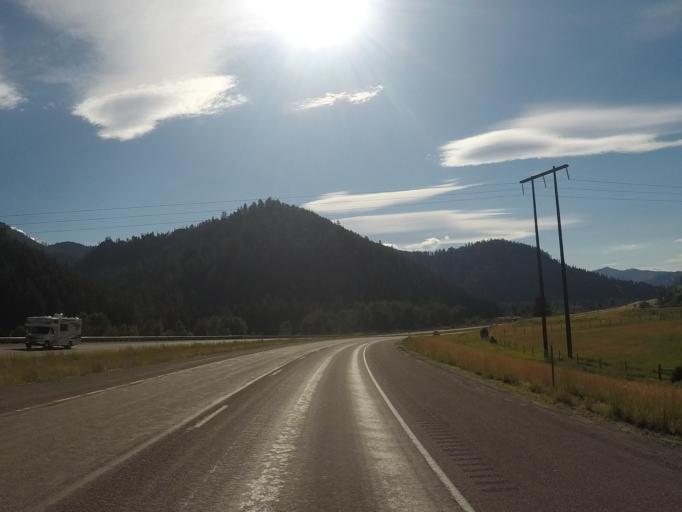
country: US
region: Montana
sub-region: Missoula County
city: Clinton
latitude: 46.6973
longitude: -113.4852
